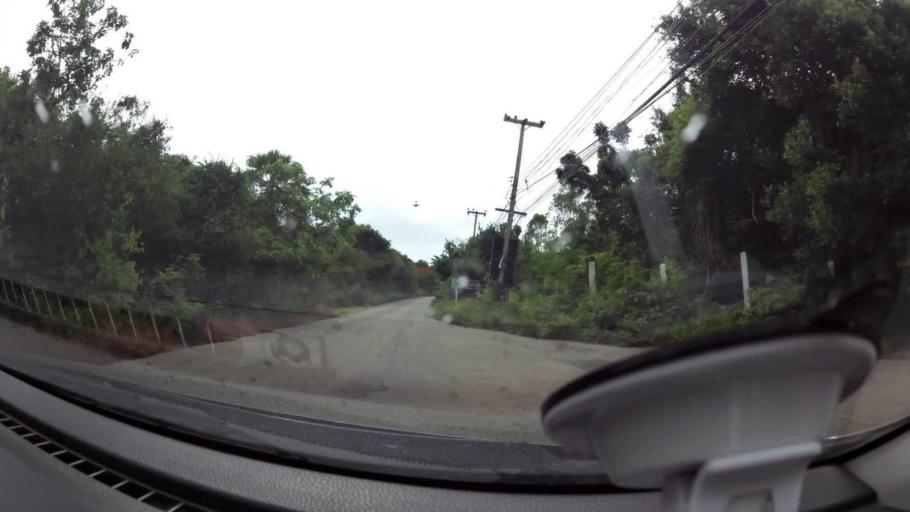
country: TH
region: Prachuap Khiri Khan
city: Pran Buri
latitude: 12.4374
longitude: 99.9727
